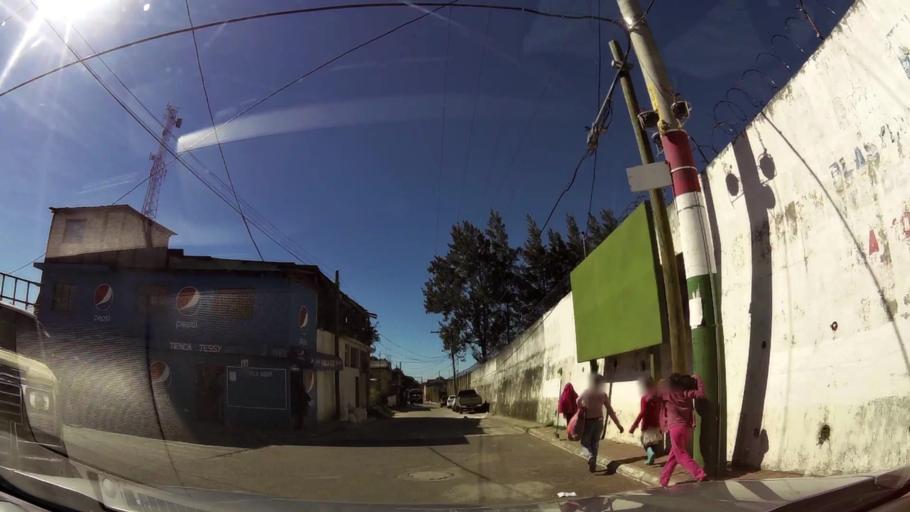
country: GT
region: Guatemala
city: Fraijanes
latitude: 14.4573
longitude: -90.4418
